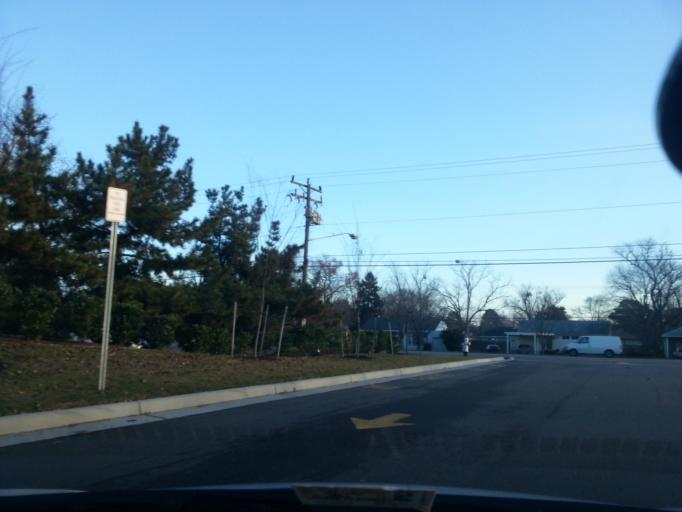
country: US
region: Virginia
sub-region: City of Norfolk
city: Norfolk
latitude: 36.8976
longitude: -76.2263
